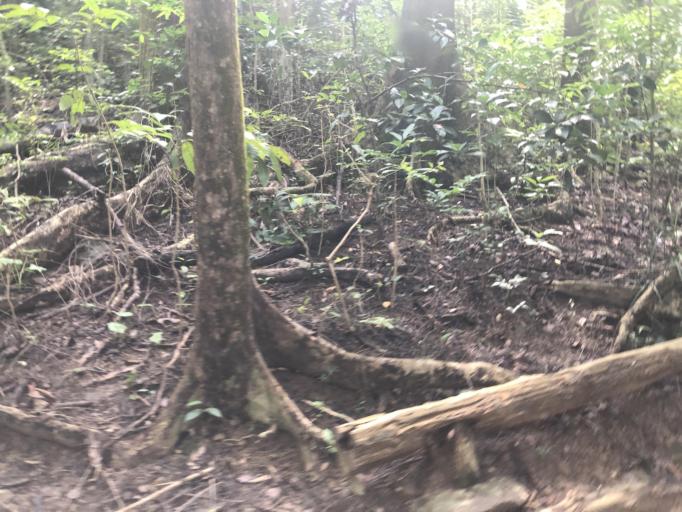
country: TW
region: Taiwan
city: Yujing
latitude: 22.9320
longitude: 120.5922
